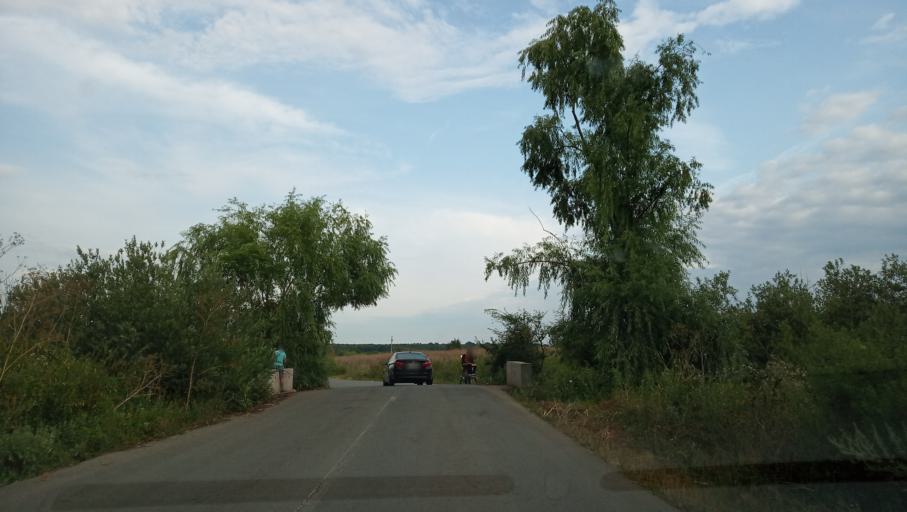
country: RO
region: Giurgiu
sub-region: Comuna Singureni
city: Singureni
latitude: 44.2292
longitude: 25.9275
